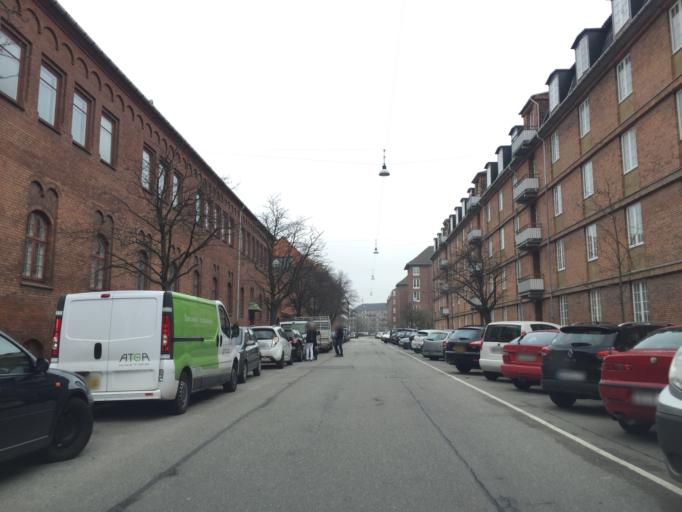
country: DK
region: Capital Region
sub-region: Kobenhavn
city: Copenhagen
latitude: 55.7078
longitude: 12.5674
